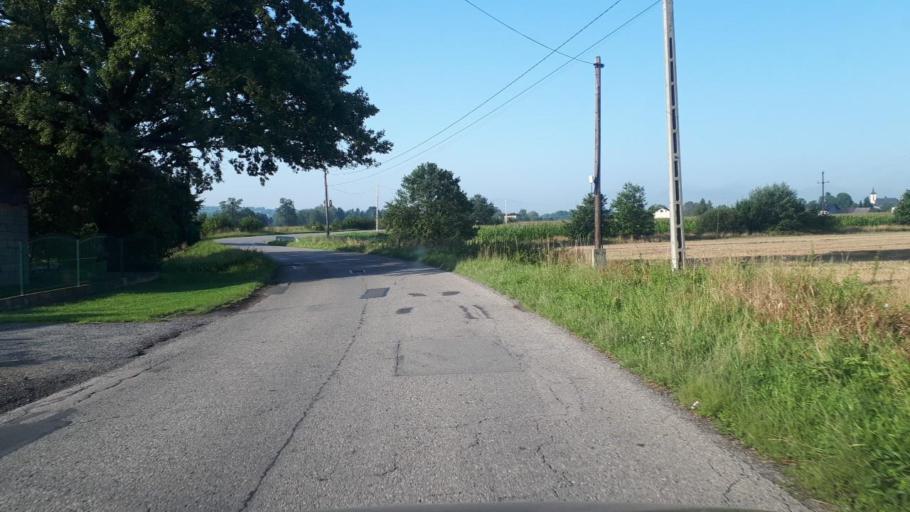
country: PL
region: Silesian Voivodeship
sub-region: Powiat cieszynski
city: Chybie
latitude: 49.8778
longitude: 18.8697
